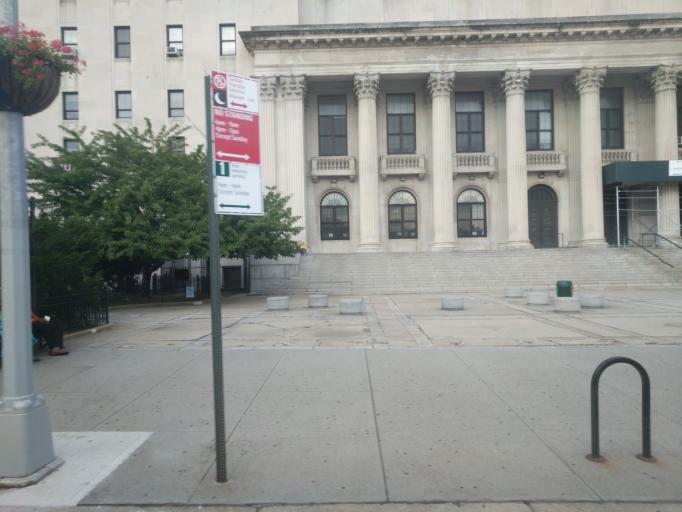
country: US
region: New York
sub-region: Queens County
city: Jamaica
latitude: 40.7044
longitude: -73.8088
